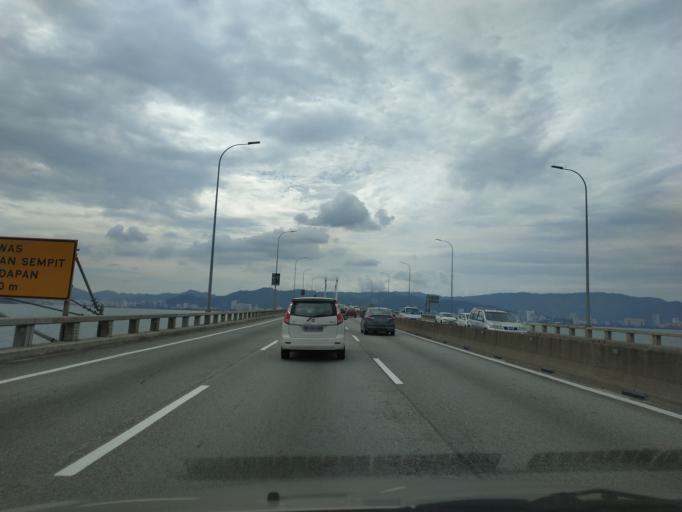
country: MY
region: Penang
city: Perai
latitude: 5.3523
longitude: 100.3579
